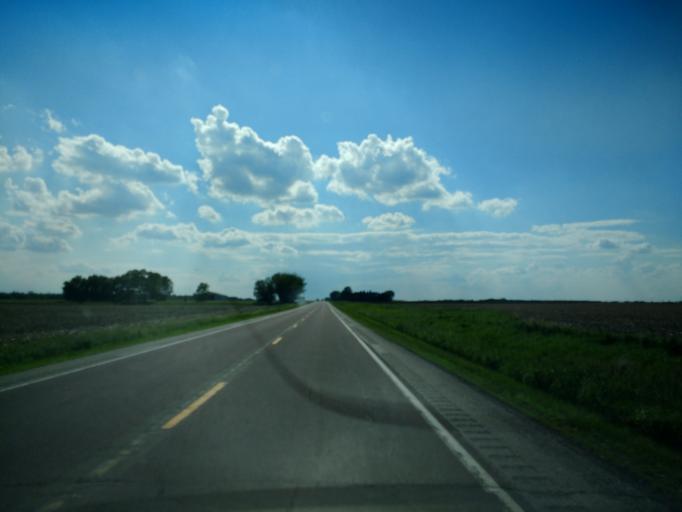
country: US
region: Iowa
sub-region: Clay County
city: Spencer
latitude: 43.1840
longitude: -95.1608
